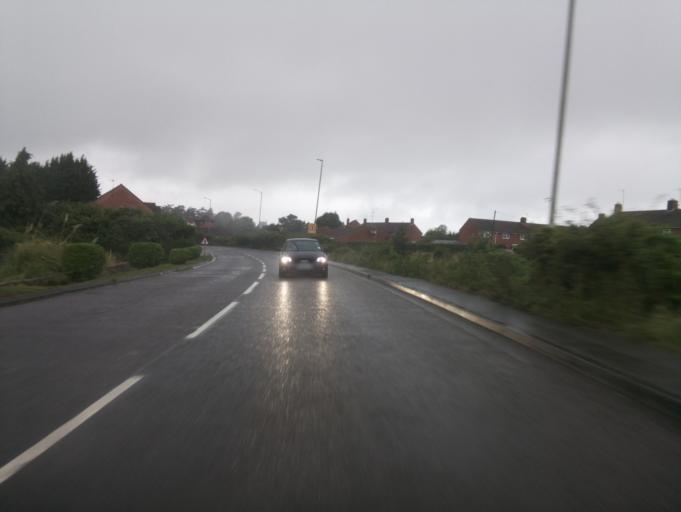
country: GB
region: England
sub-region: Gloucestershire
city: Tewkesbury
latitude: 51.9814
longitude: -2.1554
